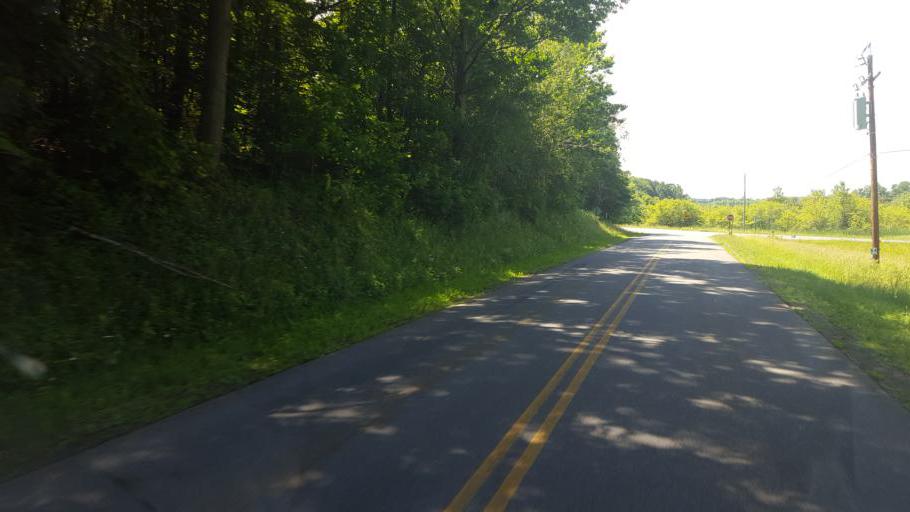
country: US
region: New York
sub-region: Wayne County
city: Wolcott
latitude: 43.2778
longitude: -76.9073
